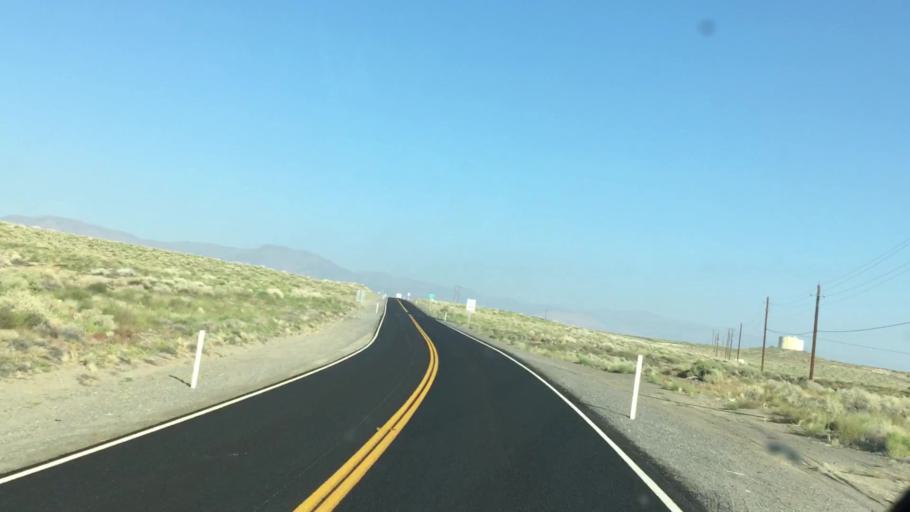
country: US
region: Nevada
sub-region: Lyon County
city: Fernley
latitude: 39.6387
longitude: -119.2928
